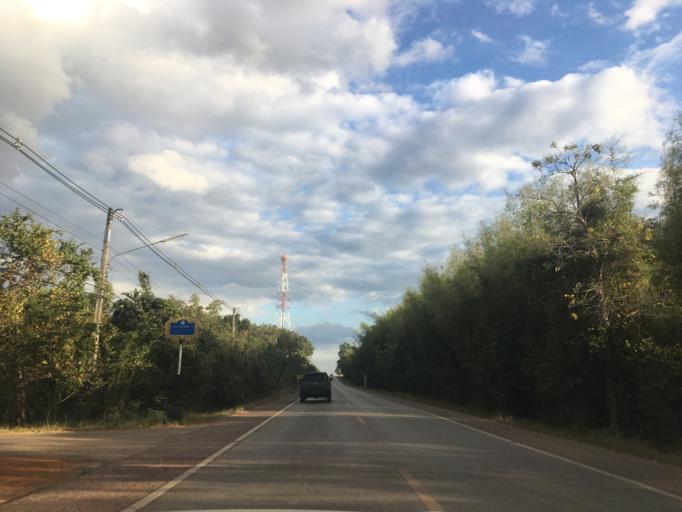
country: TH
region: Chanthaburi
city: Na Yai Am
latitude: 12.7369
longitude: 101.7422
